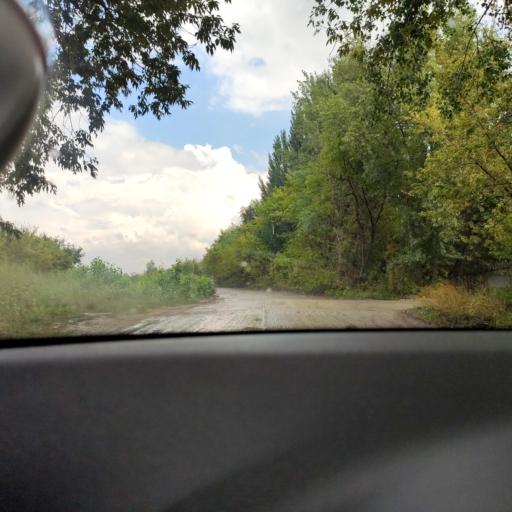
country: RU
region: Samara
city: Smyshlyayevka
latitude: 53.1947
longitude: 50.2990
